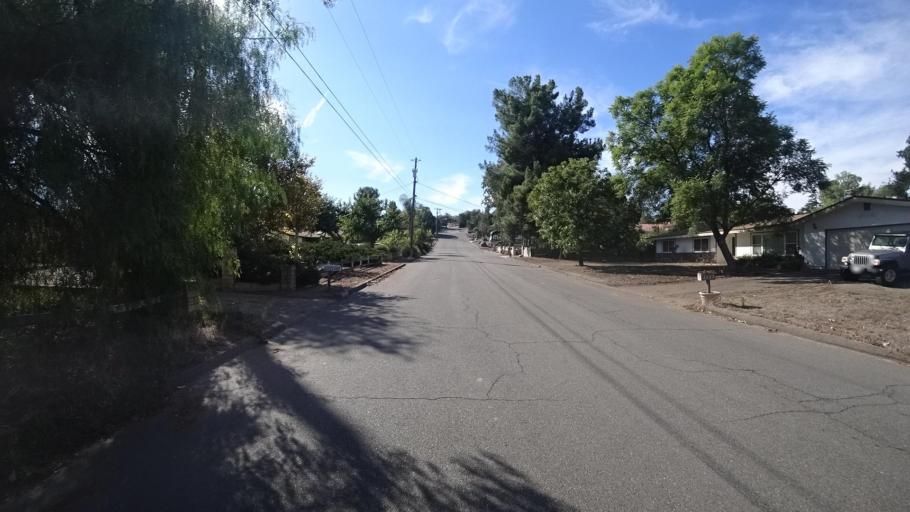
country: US
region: California
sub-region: San Diego County
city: Alpine
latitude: 32.8177
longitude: -116.7939
